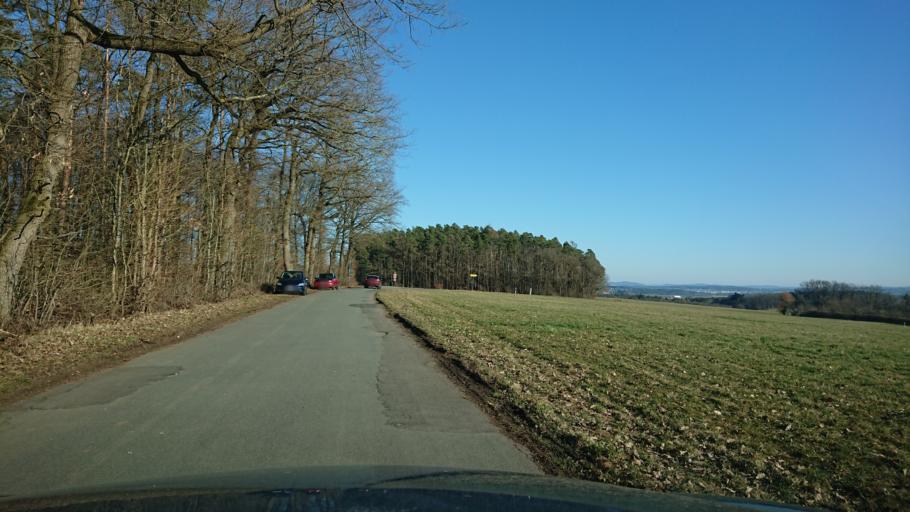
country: DE
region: Bavaria
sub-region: Upper Franconia
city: Langensendelbach
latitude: 49.6264
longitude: 11.0882
